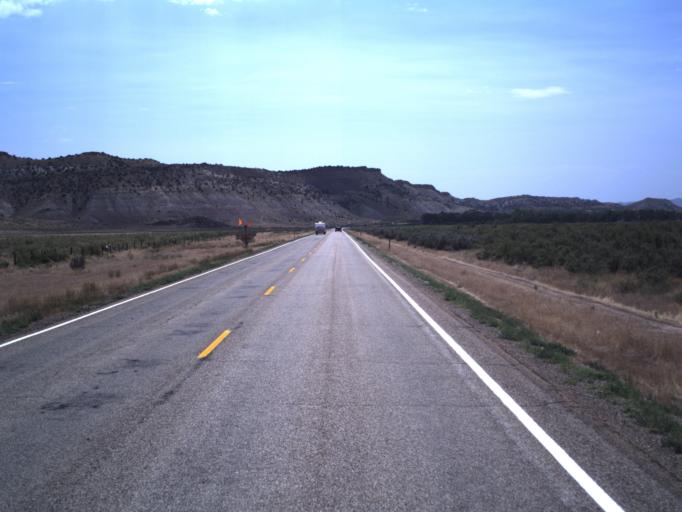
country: US
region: Utah
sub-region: Uintah County
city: Vernal
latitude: 40.5424
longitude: -109.5254
